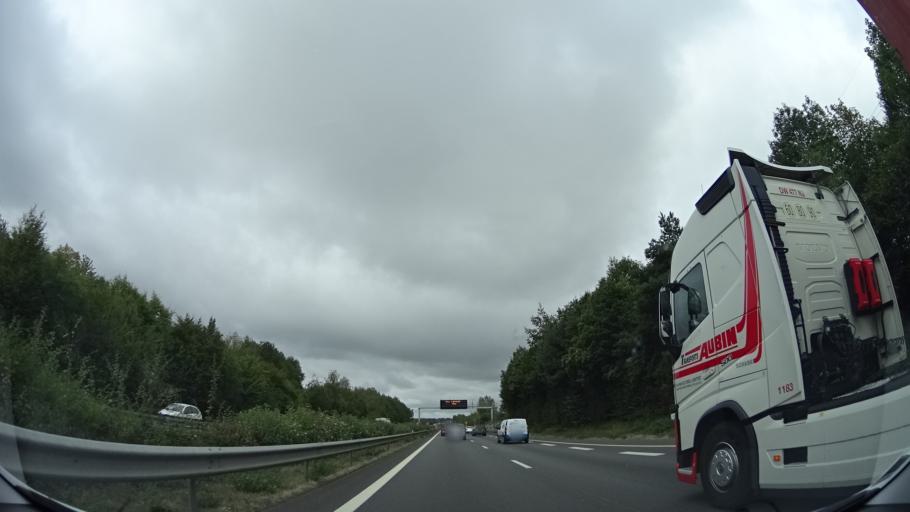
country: FR
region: Brittany
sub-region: Departement d'Ille-et-Vilaine
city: Saint-Gregoire
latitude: 48.1420
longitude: -1.6697
